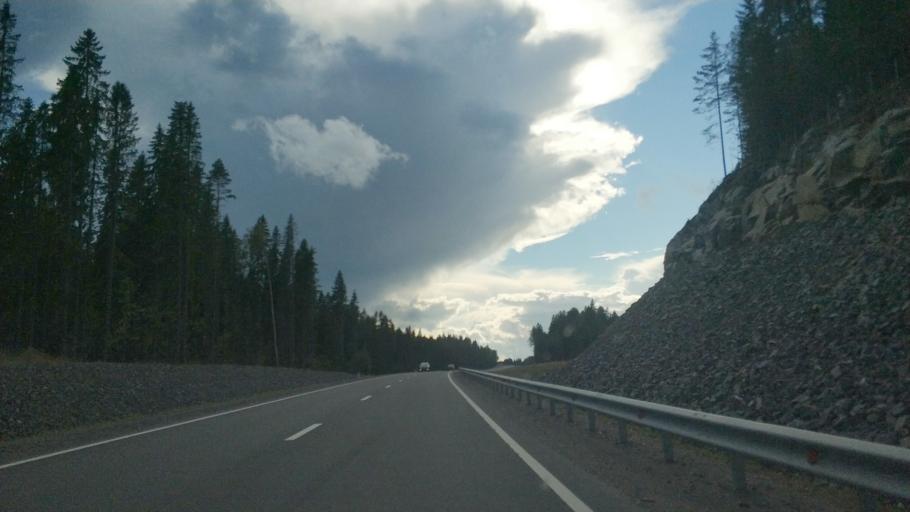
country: RU
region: Republic of Karelia
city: Lakhdenpokh'ya
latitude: 61.5084
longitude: 30.0602
